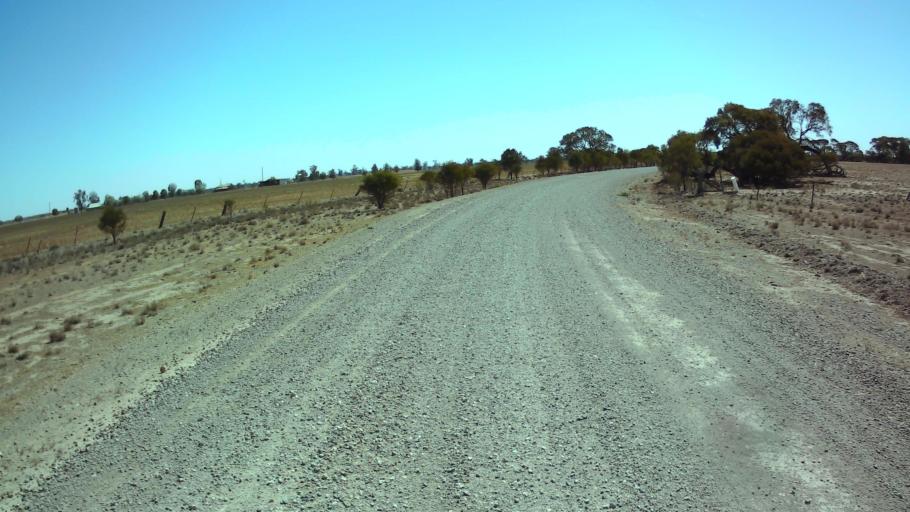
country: AU
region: New South Wales
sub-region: Forbes
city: Forbes
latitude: -33.7452
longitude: 147.7400
